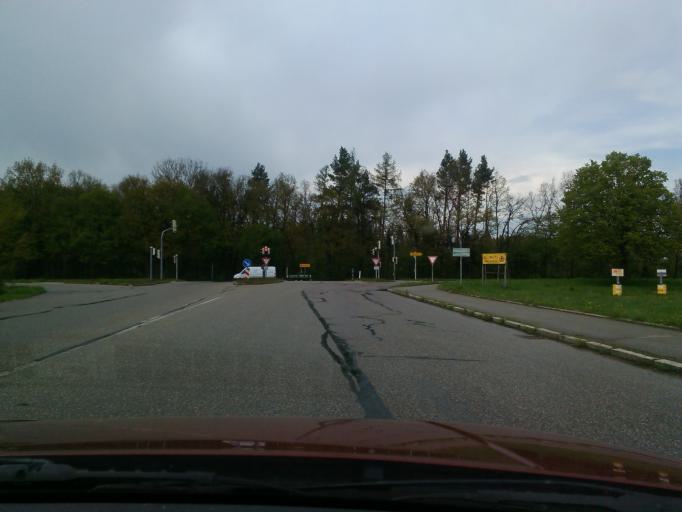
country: DE
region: Bavaria
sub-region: Upper Bavaria
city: Neuried
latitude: 48.1137
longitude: 11.4615
